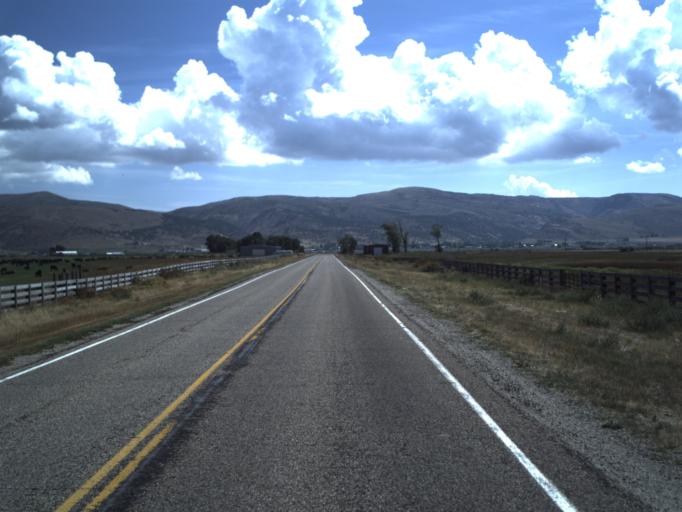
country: US
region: Utah
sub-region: Rich County
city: Randolph
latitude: 41.8426
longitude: -111.3471
